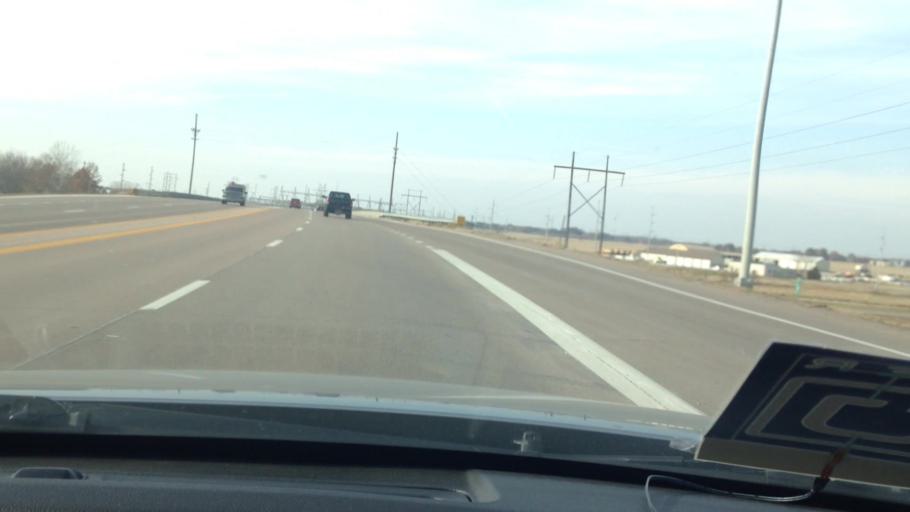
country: US
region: Missouri
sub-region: Henry County
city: Clinton
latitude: 38.3850
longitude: -93.7538
